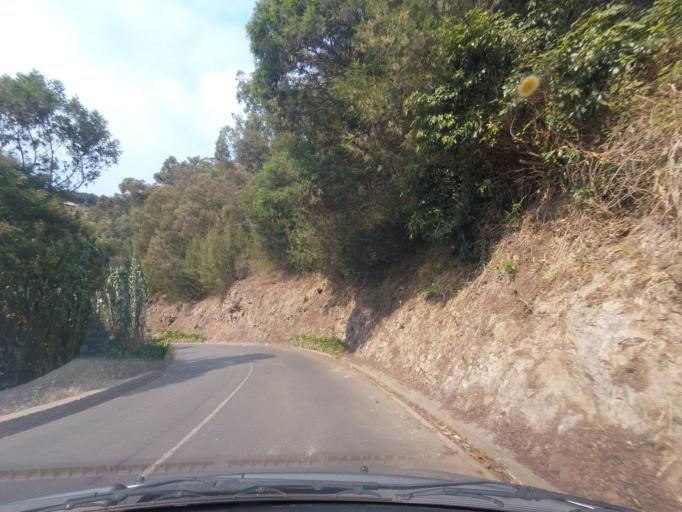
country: PT
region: Madeira
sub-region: Ribeira Brava
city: Campanario
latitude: 32.6915
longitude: -17.0581
